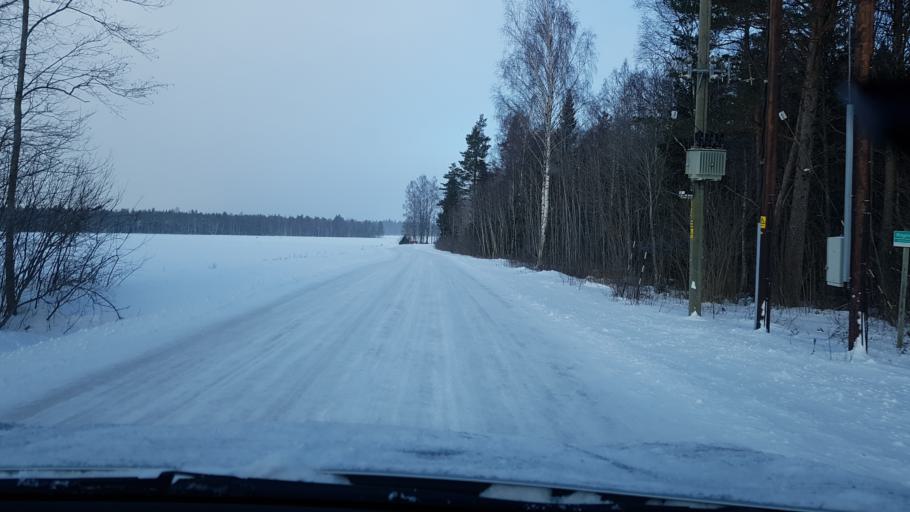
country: EE
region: Harju
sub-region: Nissi vald
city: Turba
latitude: 59.1953
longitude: 24.1396
